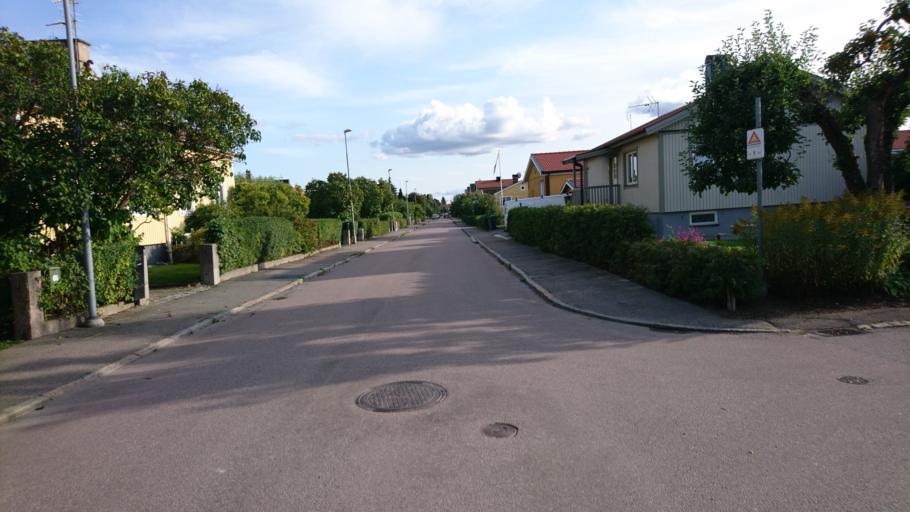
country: SE
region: Uppsala
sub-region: Uppsala Kommun
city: Uppsala
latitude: 59.8773
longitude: 17.6341
